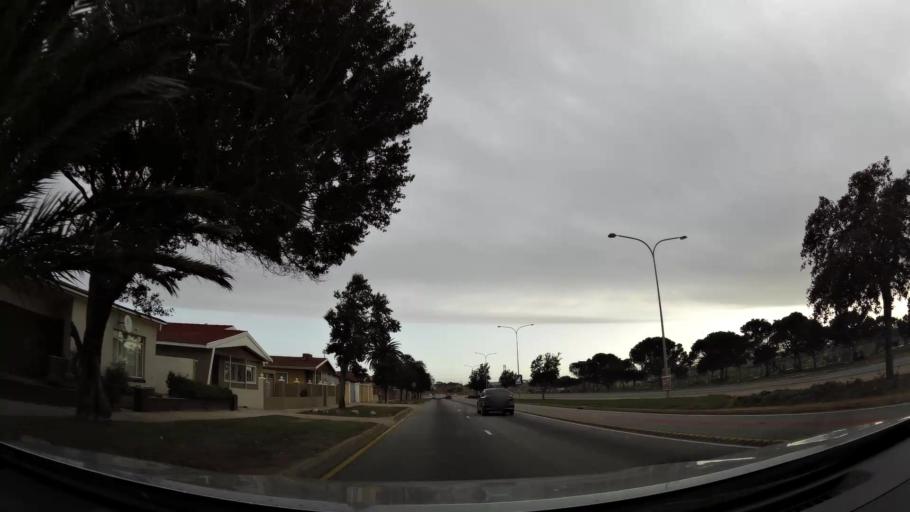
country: ZA
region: Eastern Cape
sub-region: Nelson Mandela Bay Metropolitan Municipality
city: Port Elizabeth
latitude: -33.9169
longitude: 25.5635
